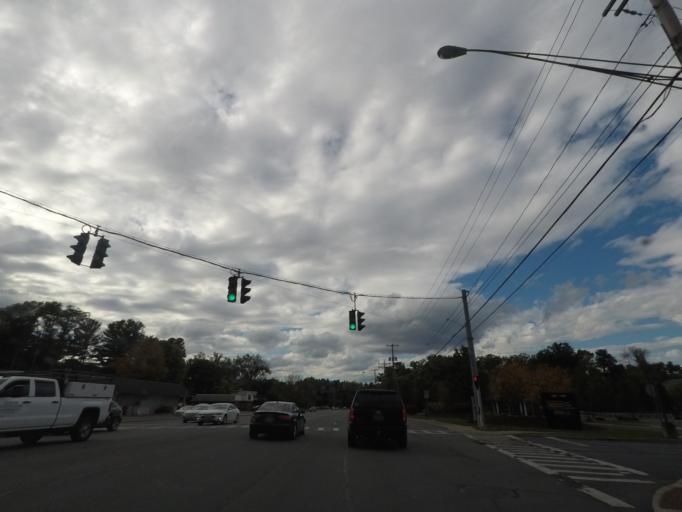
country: US
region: New York
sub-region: Albany County
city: Westmere
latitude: 42.6926
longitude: -73.8739
